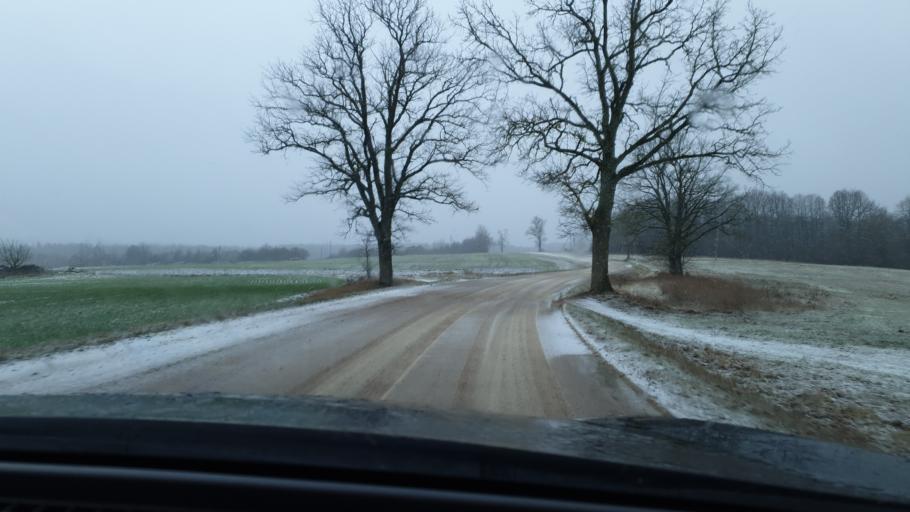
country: LT
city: Jieznas
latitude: 54.5600
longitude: 24.3173
